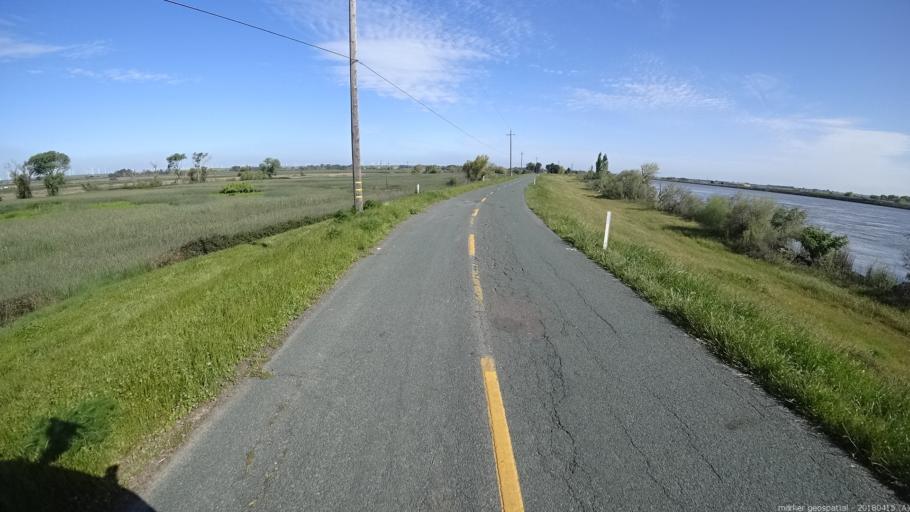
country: US
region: California
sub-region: Solano County
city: Rio Vista
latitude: 38.0864
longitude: -121.6869
